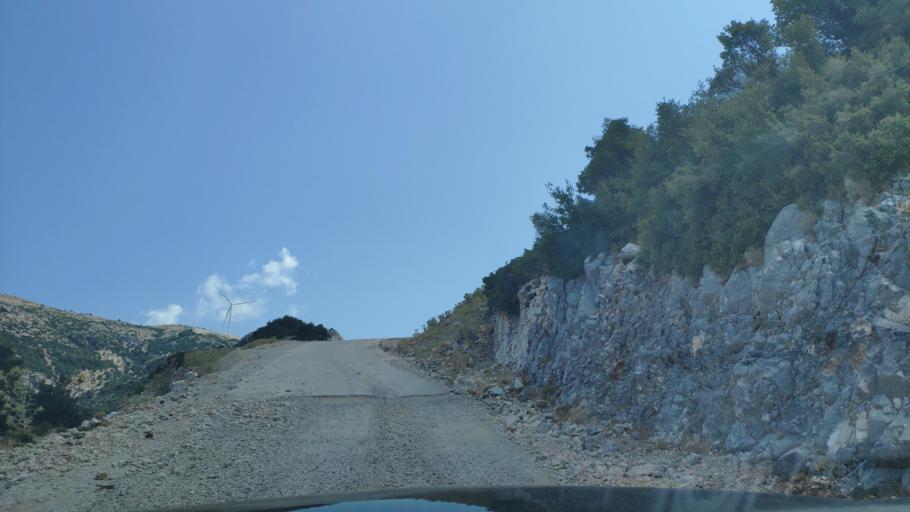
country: GR
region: West Greece
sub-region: Nomos Aitolias kai Akarnanias
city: Monastirakion
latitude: 38.7860
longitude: 20.9787
